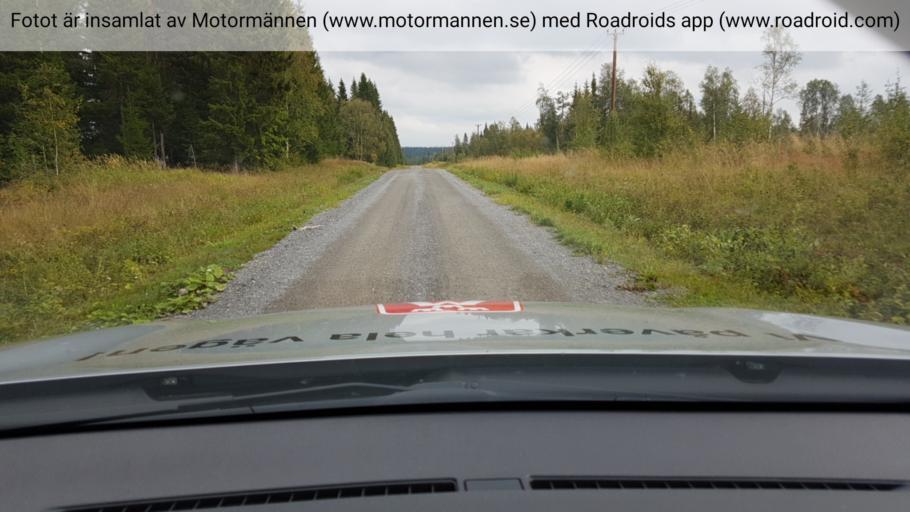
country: SE
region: Jaemtland
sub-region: Stroemsunds Kommun
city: Stroemsund
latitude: 63.7834
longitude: 15.2543
